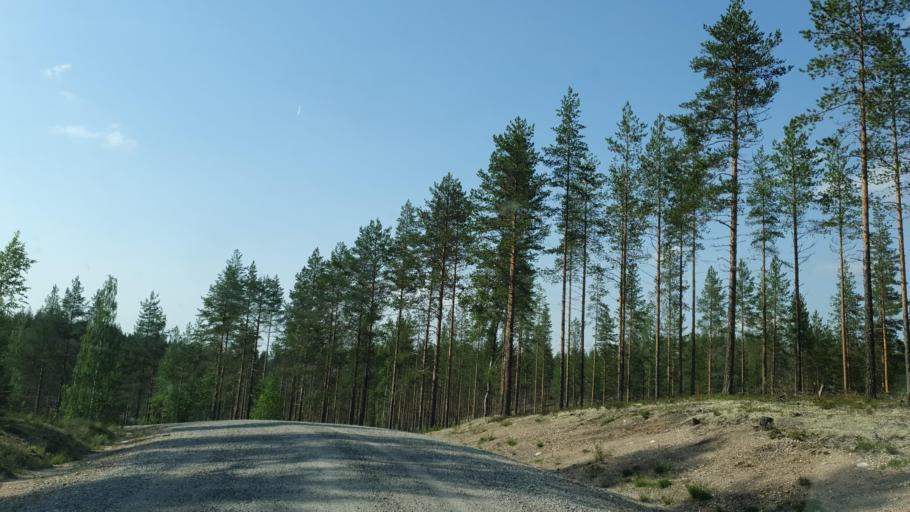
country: FI
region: Kainuu
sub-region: Kehys-Kainuu
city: Kuhmo
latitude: 64.0204
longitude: 29.9044
